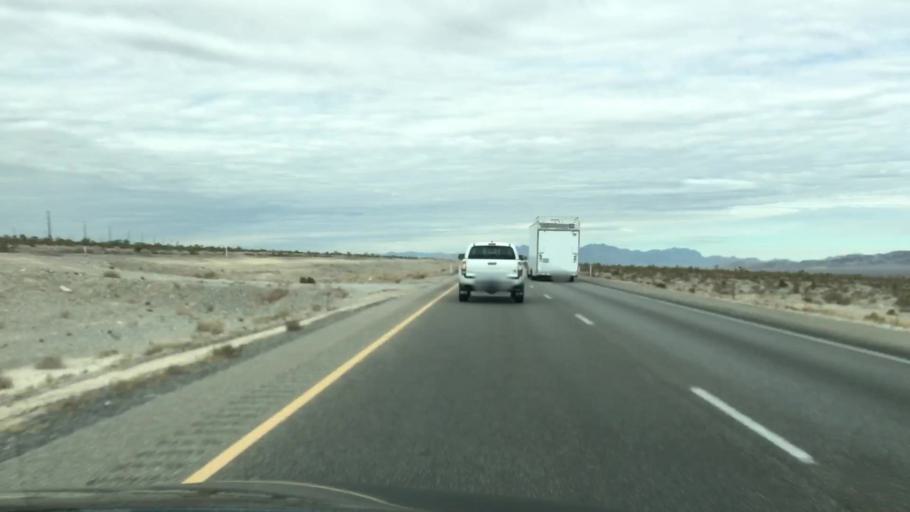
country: US
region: Nevada
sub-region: Clark County
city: Summerlin South
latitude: 36.4507
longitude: -115.4379
